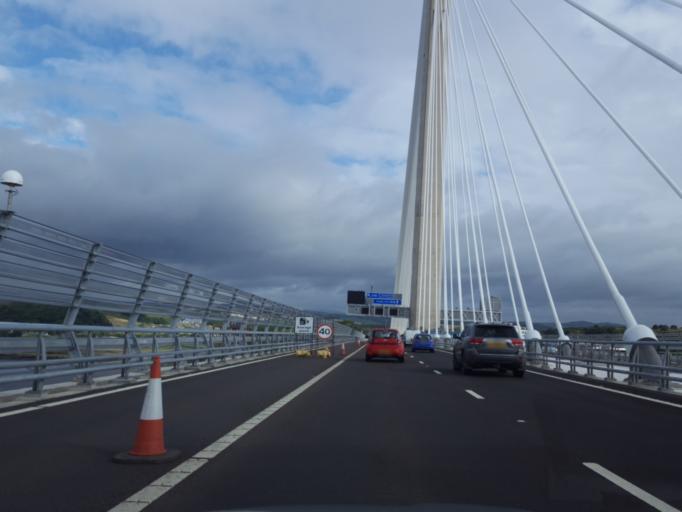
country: GB
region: Scotland
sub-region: Fife
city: North Queensferry
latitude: 56.0087
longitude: -3.4102
